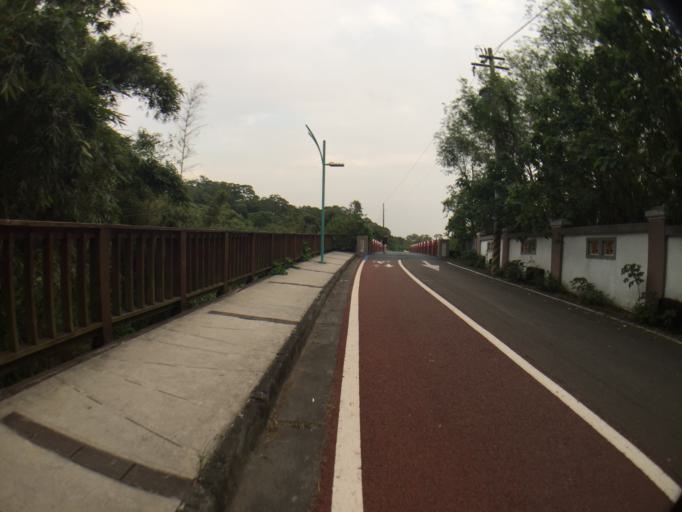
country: TW
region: Taiwan
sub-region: Hsinchu
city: Hsinchu
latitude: 24.7725
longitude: 120.9754
